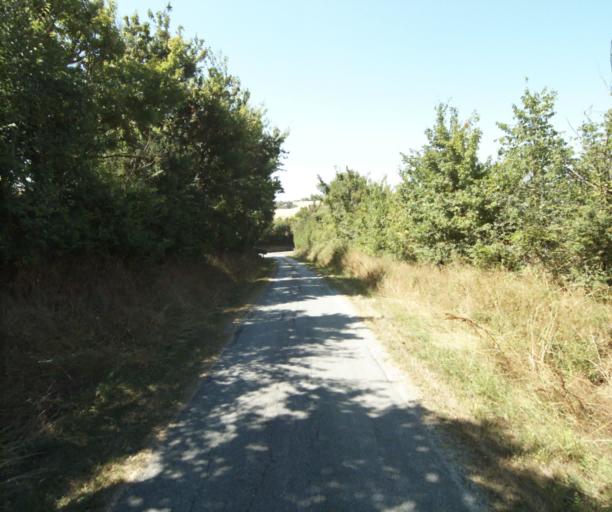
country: FR
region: Midi-Pyrenees
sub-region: Departement de la Haute-Garonne
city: Saint-Felix-Lauragais
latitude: 43.4914
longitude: 1.8938
